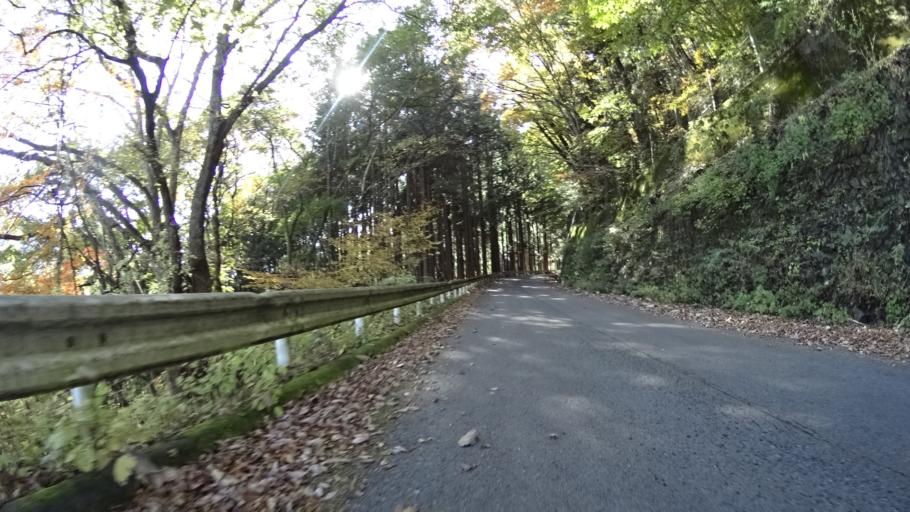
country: JP
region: Yamanashi
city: Otsuki
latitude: 35.7444
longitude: 138.9601
